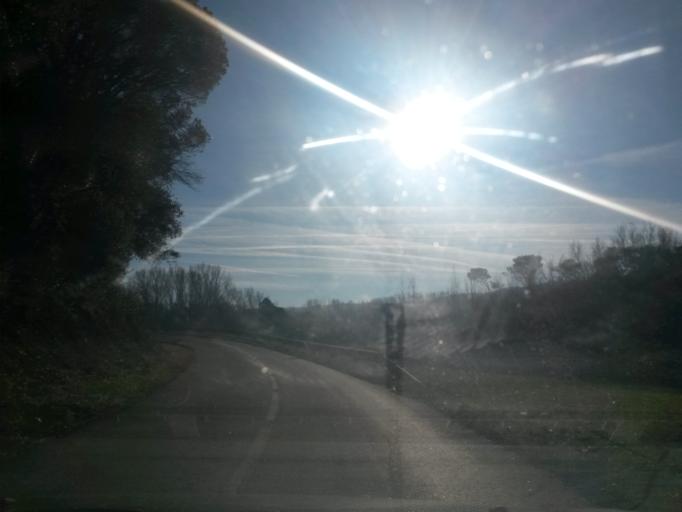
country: ES
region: Catalonia
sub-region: Provincia de Girona
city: Angles
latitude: 41.9780
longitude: 2.6744
